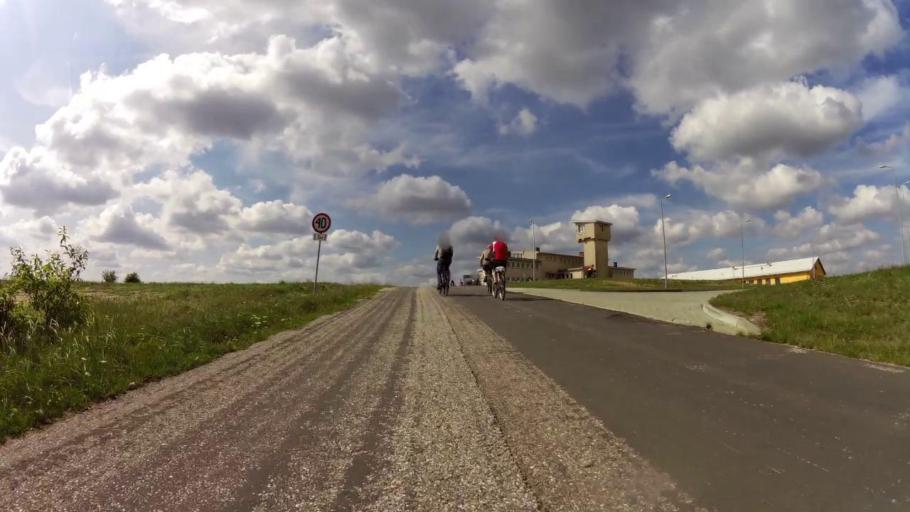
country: PL
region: West Pomeranian Voivodeship
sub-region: Powiat drawski
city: Drawsko Pomorskie
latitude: 53.4555
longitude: 15.7755
